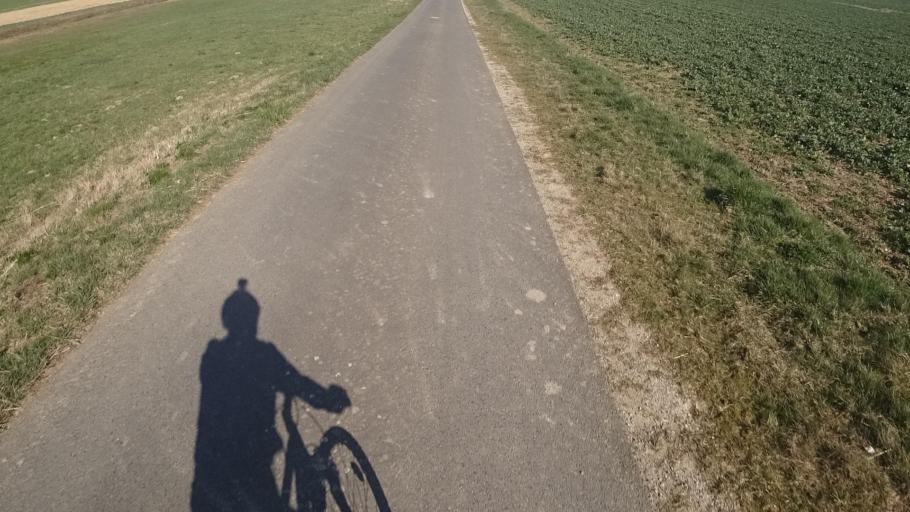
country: DE
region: Rheinland-Pfalz
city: Schnorbach
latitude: 49.9924
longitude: 7.6447
